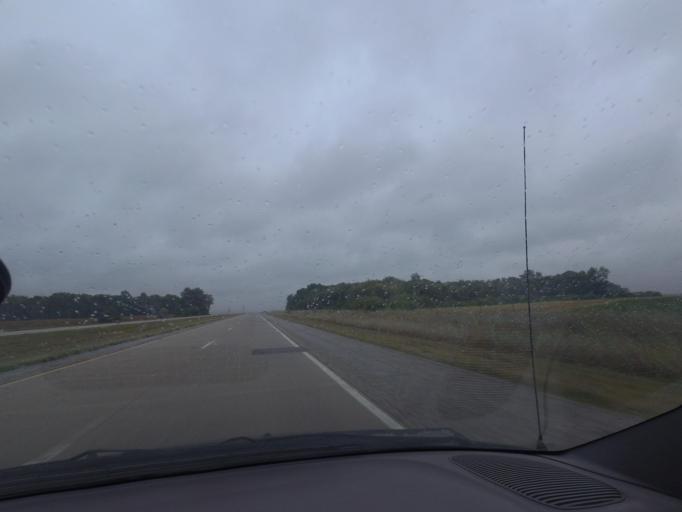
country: US
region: Illinois
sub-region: Adams County
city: Payson
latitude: 39.7379
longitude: -91.2522
